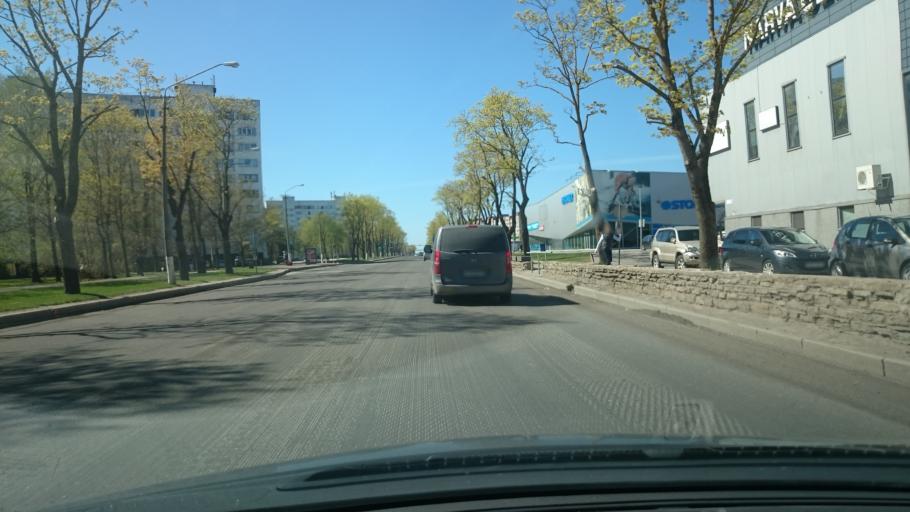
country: EE
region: Ida-Virumaa
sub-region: Narva linn
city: Narva
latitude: 59.3811
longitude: 28.1730
